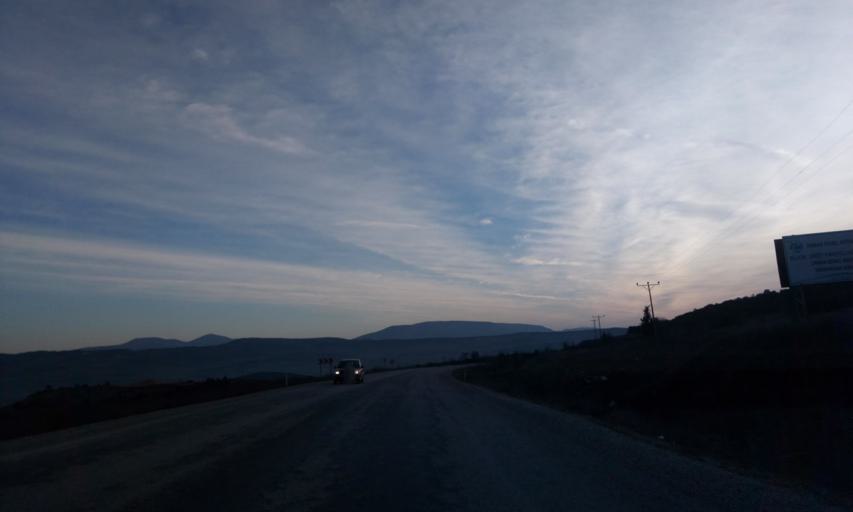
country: TR
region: Bilecik
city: Kuplu
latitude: 40.1238
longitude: 30.0247
